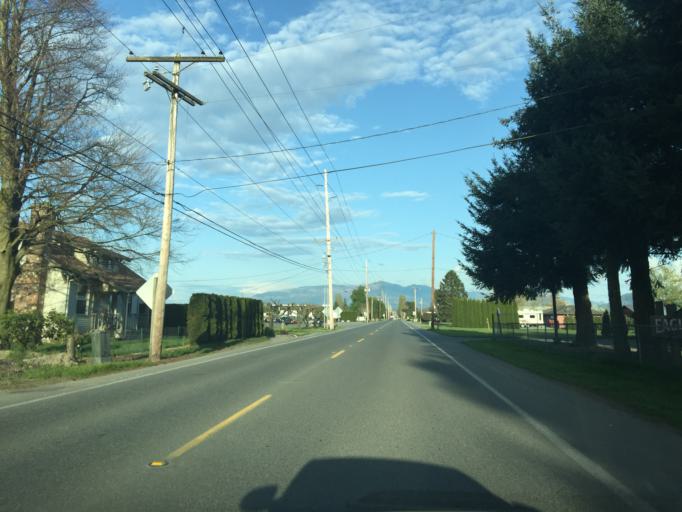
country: US
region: Washington
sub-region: Skagit County
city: Mount Vernon
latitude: 48.4209
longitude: -122.3988
